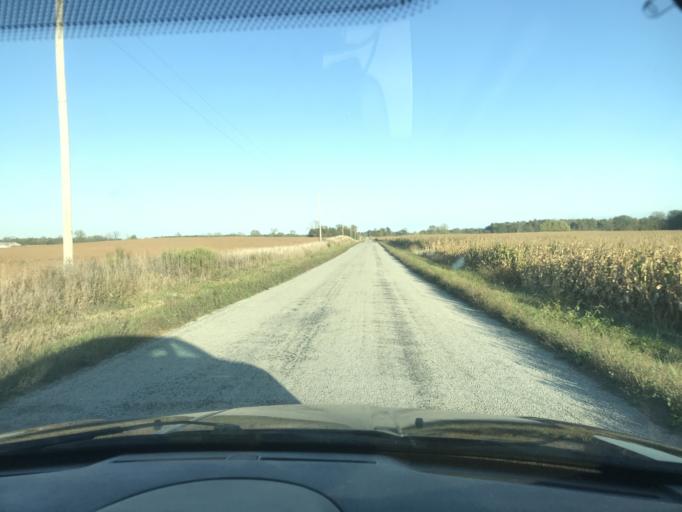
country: US
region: Ohio
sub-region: Logan County
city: West Liberty
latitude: 40.2339
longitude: -83.8408
